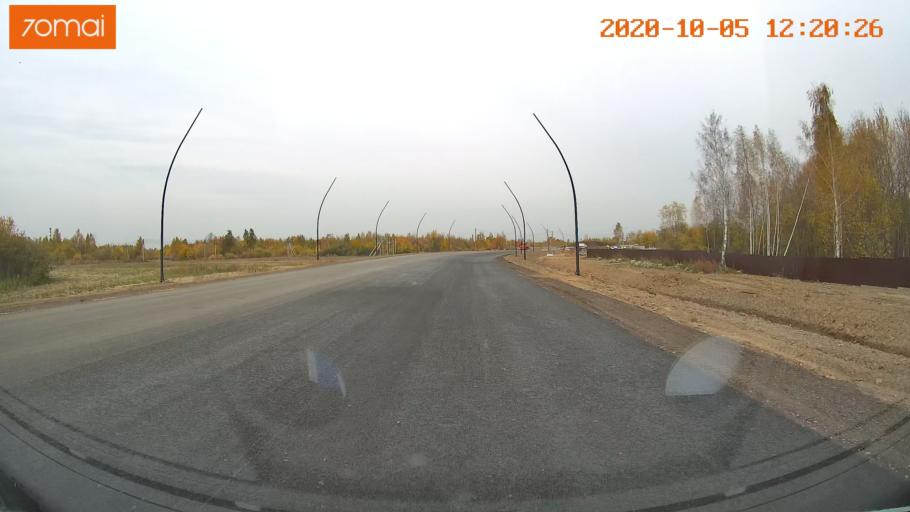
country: RU
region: Ivanovo
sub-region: Gorod Ivanovo
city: Ivanovo
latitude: 56.9635
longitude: 40.9307
